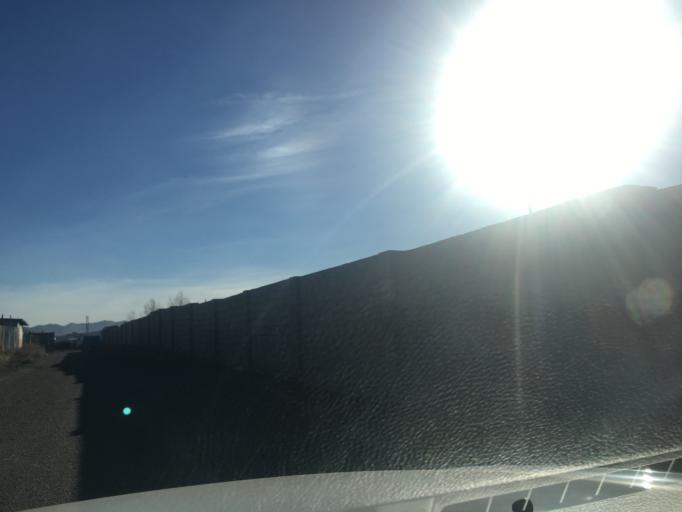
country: MN
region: Ulaanbaatar
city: Ulaanbaatar
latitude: 47.9017
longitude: 106.7754
